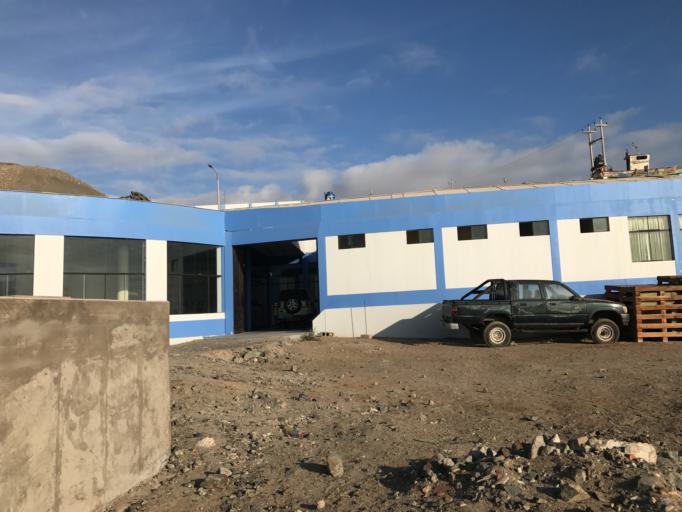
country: PE
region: Moquegua
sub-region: Provincia de Ilo
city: Ilo
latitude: -17.6705
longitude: -71.3624
